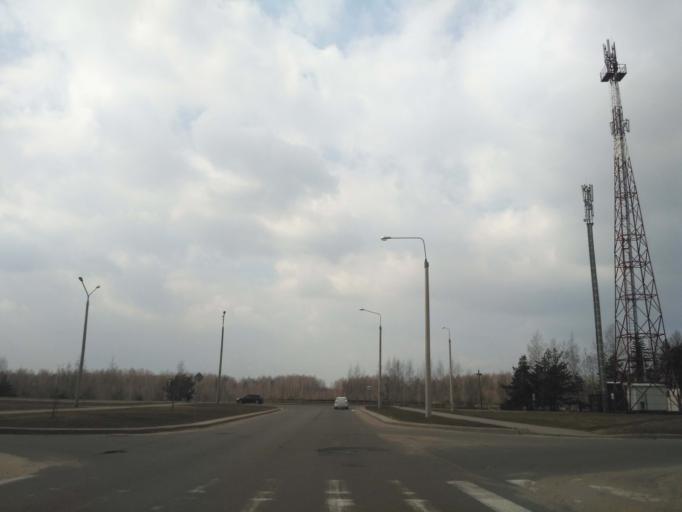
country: BY
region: Minsk
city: Horad Barysaw
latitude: 54.2167
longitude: 28.4705
